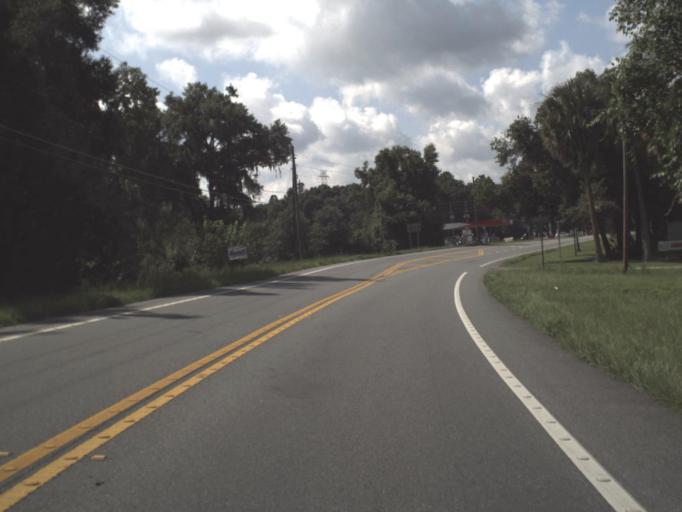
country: US
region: Florida
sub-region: Citrus County
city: Citrus Springs
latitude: 28.9681
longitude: -82.4190
